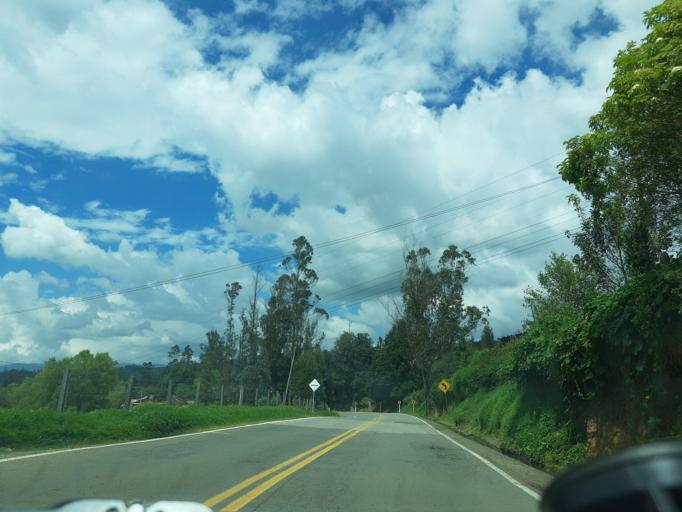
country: CO
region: Boyaca
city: Sutamarchan
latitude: 5.5981
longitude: -73.7167
